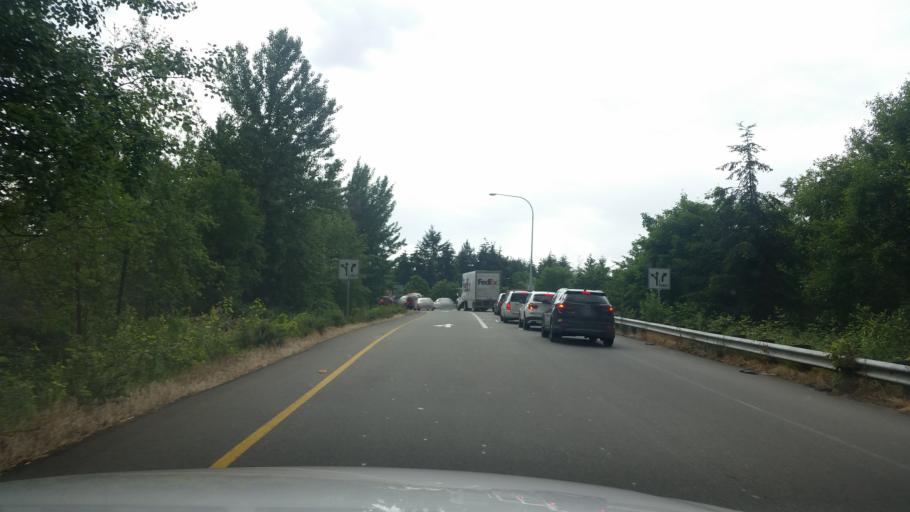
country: US
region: Washington
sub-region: Snohomish County
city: Mountlake Terrace
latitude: 47.8006
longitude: -122.3151
